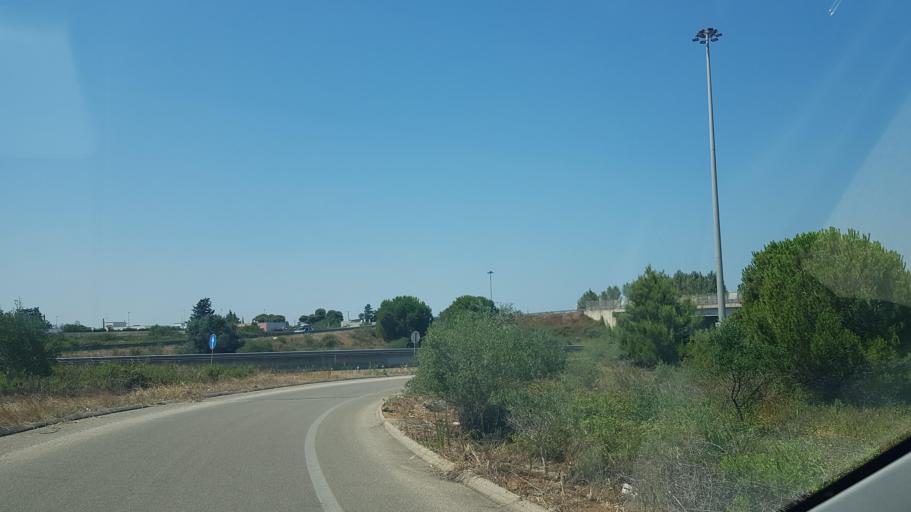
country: IT
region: Apulia
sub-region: Provincia di Lecce
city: Merine
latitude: 40.3413
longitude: 18.2027
